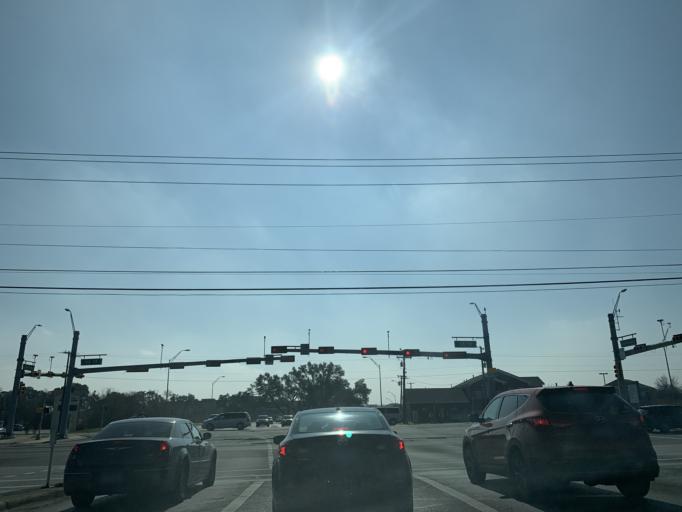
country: US
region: Texas
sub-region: Williamson County
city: Round Rock
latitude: 30.5185
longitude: -97.6556
